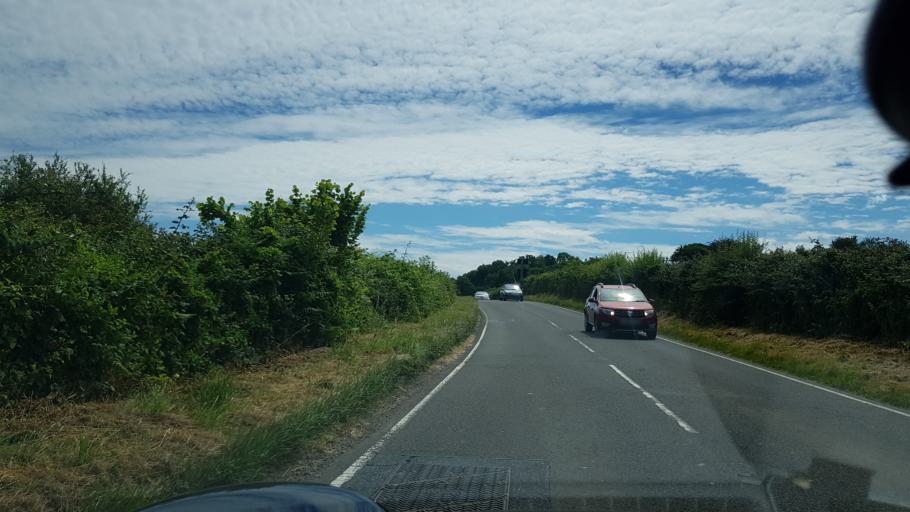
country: GB
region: Wales
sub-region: Carmarthenshire
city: Saint Clears
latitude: 51.8027
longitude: -4.4942
